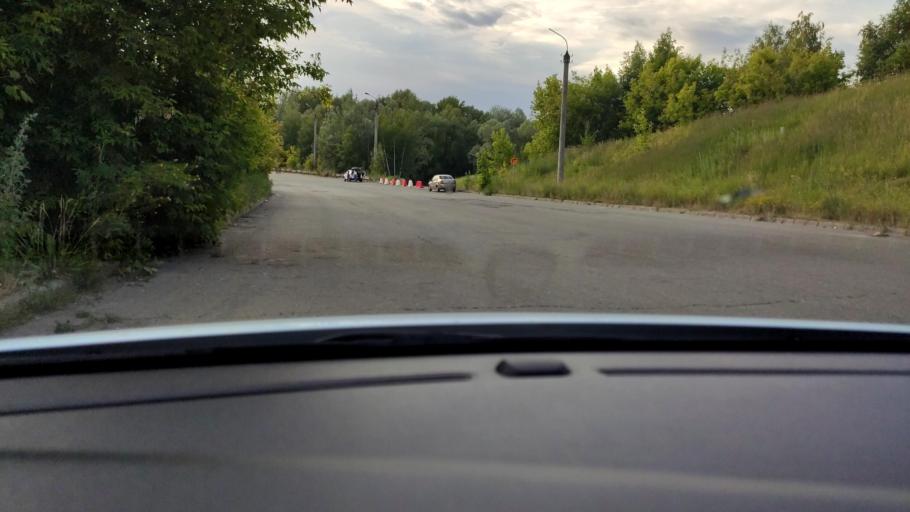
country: RU
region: Tatarstan
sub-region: Gorod Kazan'
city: Kazan
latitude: 55.8229
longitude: 49.1732
